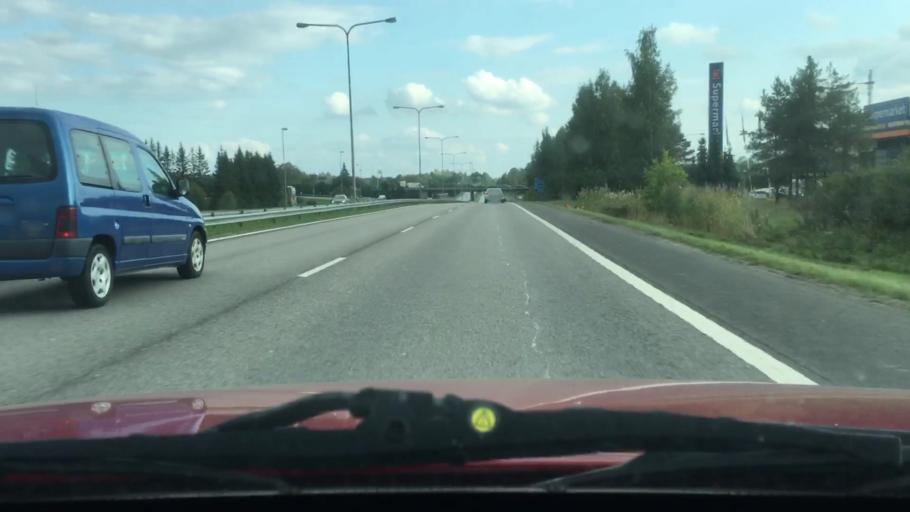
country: FI
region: Varsinais-Suomi
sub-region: Turku
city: Raisio
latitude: 60.4912
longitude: 22.1706
